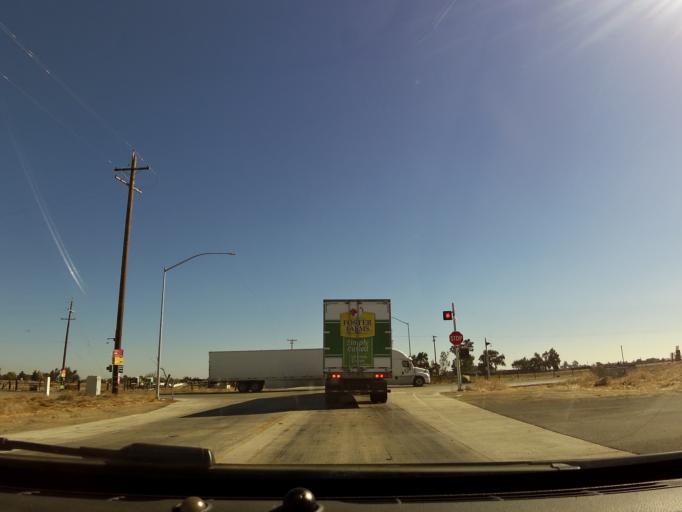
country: US
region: California
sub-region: Merced County
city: Hilmar-Irwin
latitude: 37.3131
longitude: -120.8518
